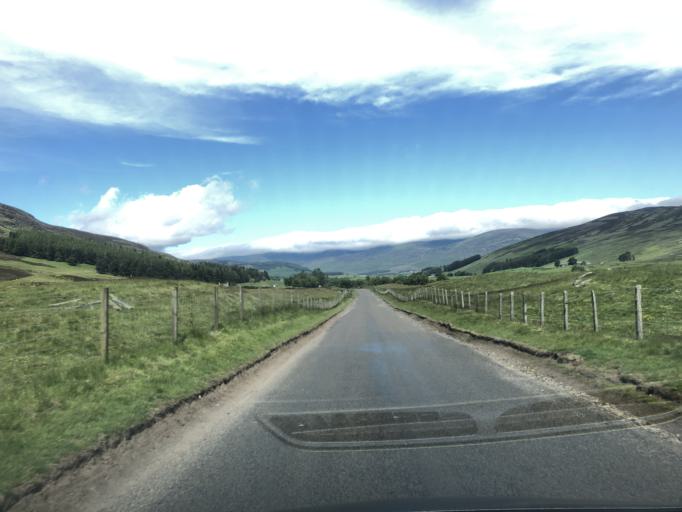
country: GB
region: Scotland
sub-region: Angus
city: Kirriemuir
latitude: 56.7688
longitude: -3.0245
